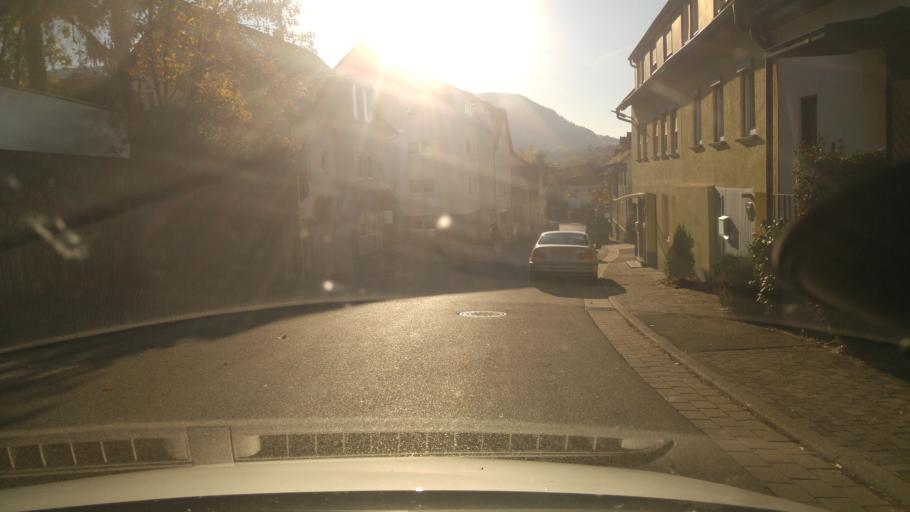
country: DE
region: Baden-Wuerttemberg
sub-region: Regierungsbezirk Stuttgart
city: Owen
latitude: 48.5874
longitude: 9.4524
